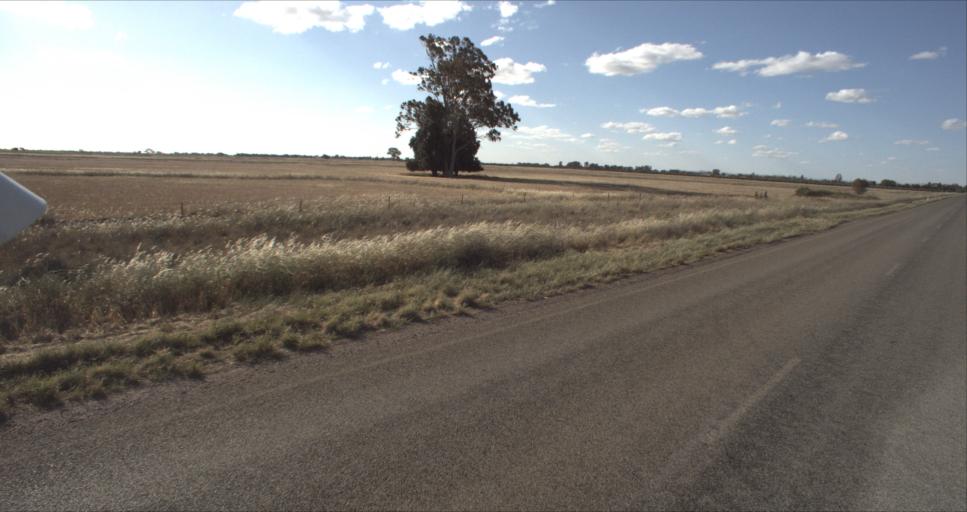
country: AU
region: New South Wales
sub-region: Leeton
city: Leeton
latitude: -34.5365
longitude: 146.2804
